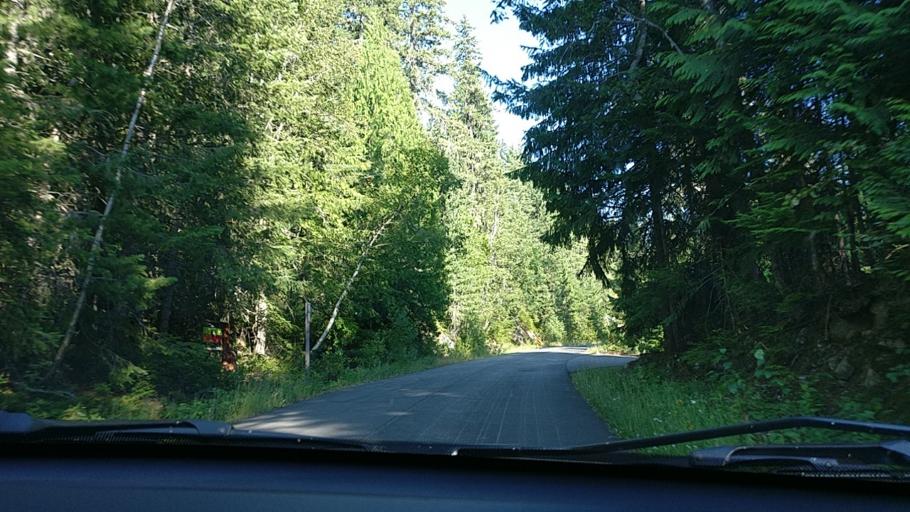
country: CA
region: British Columbia
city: Revelstoke
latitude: 51.0104
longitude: -118.1852
